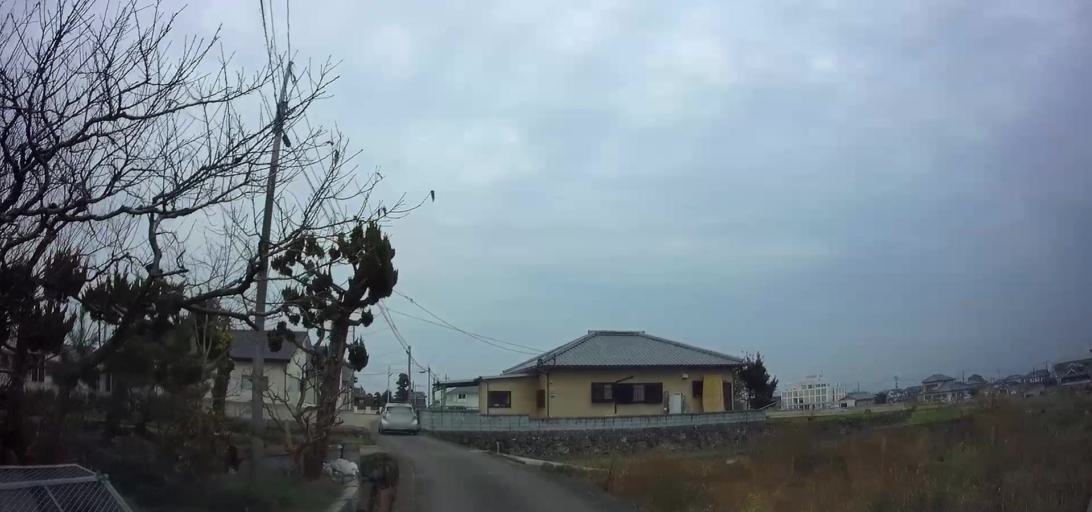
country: JP
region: Nagasaki
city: Shimabara
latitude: 32.6641
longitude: 130.2985
